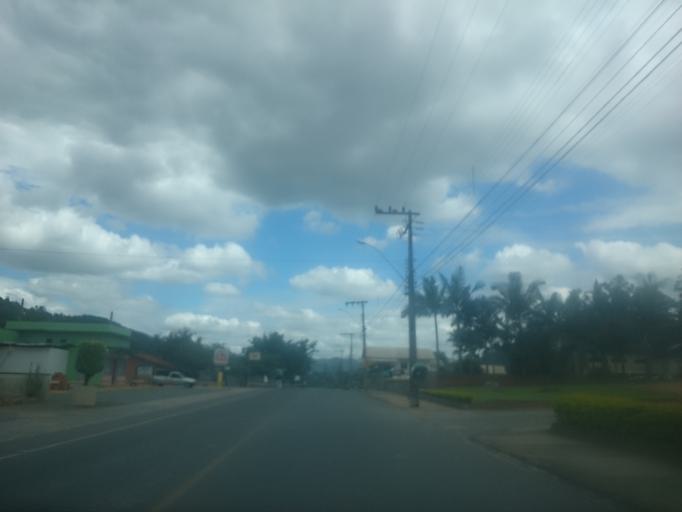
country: BR
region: Santa Catarina
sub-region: Pomerode
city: Pomerode
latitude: -26.7156
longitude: -49.1669
